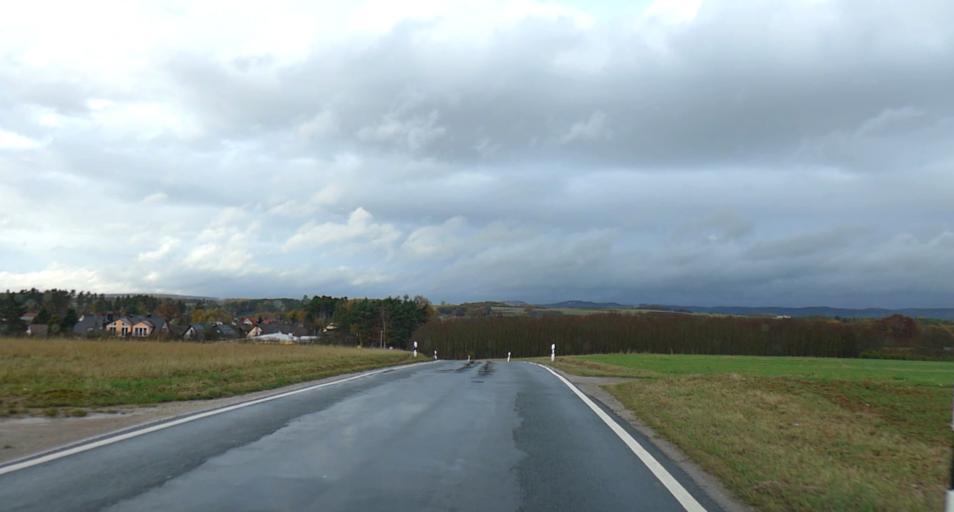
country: DE
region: Bavaria
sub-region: Upper Franconia
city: Effeltrich
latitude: 49.6531
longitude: 11.0867
